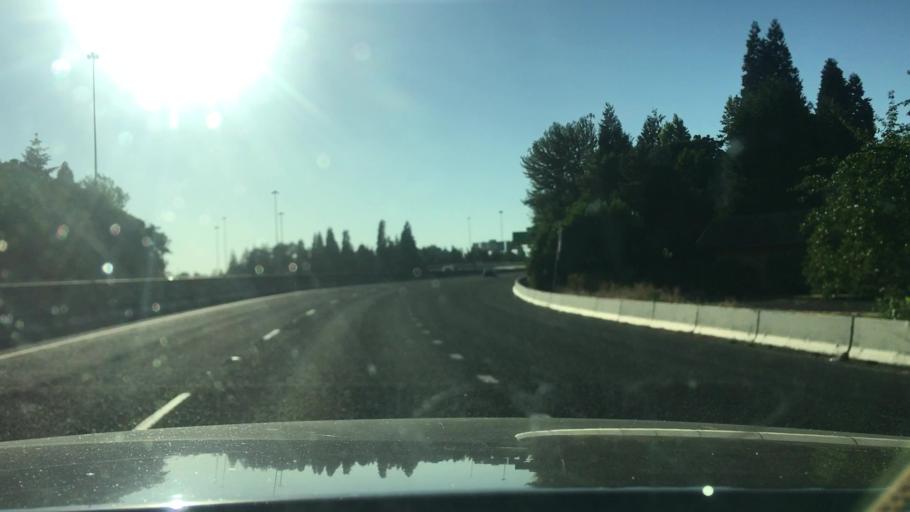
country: US
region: Oregon
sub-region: Lane County
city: Eugene
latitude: 44.0631
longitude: -123.0942
